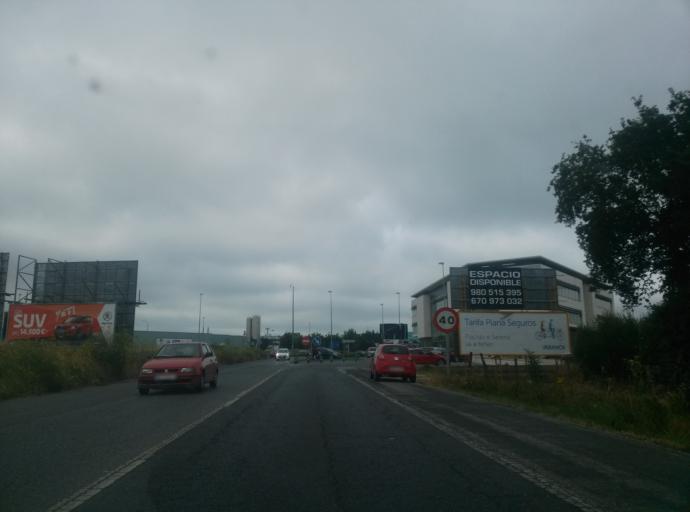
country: ES
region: Galicia
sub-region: Provincia de Lugo
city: Lugo
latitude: 43.0423
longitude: -7.5691
